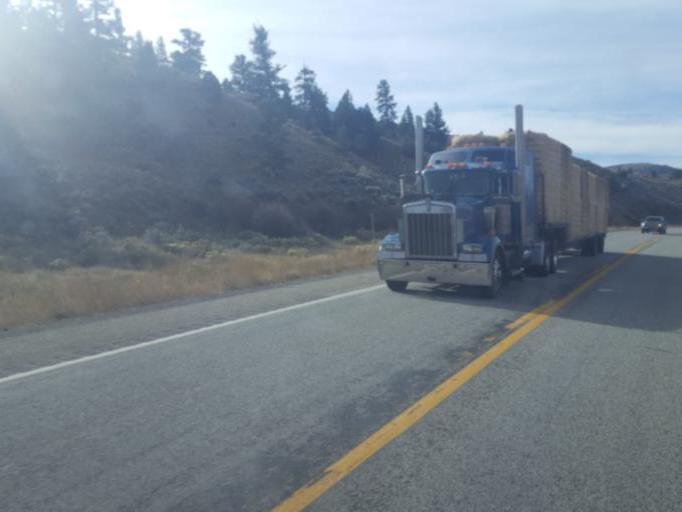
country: US
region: Colorado
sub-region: Costilla County
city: San Luis
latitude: 37.5198
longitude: -105.3002
